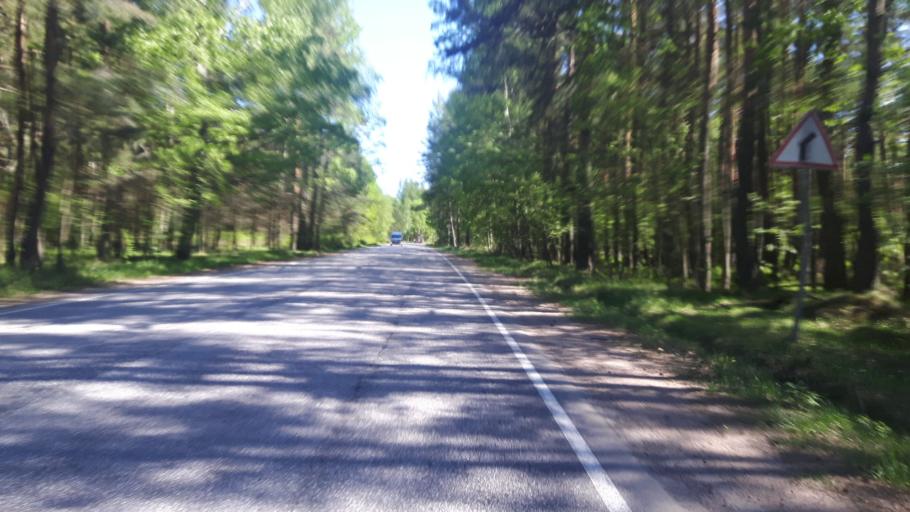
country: RU
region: Leningrad
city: Glebychevo
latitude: 60.2874
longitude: 28.8742
